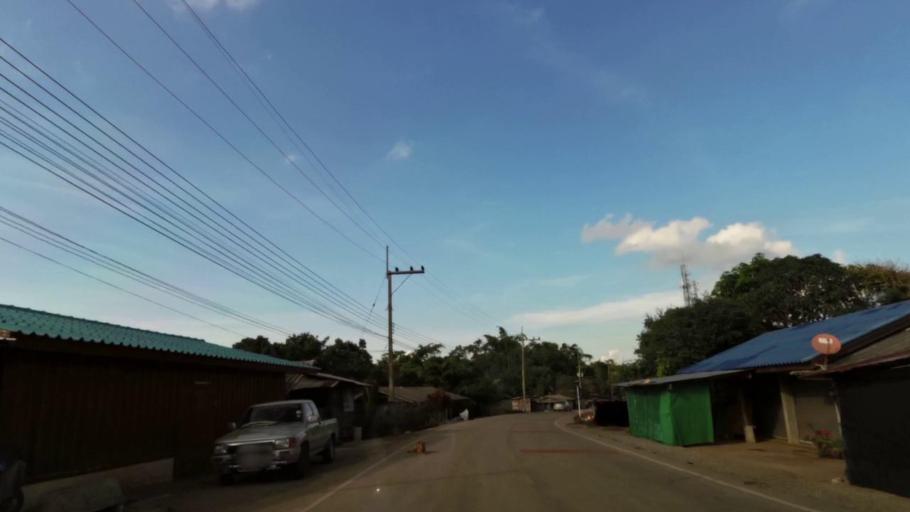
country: TH
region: Chiang Rai
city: Khun Tan
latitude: 19.8685
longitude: 100.3395
